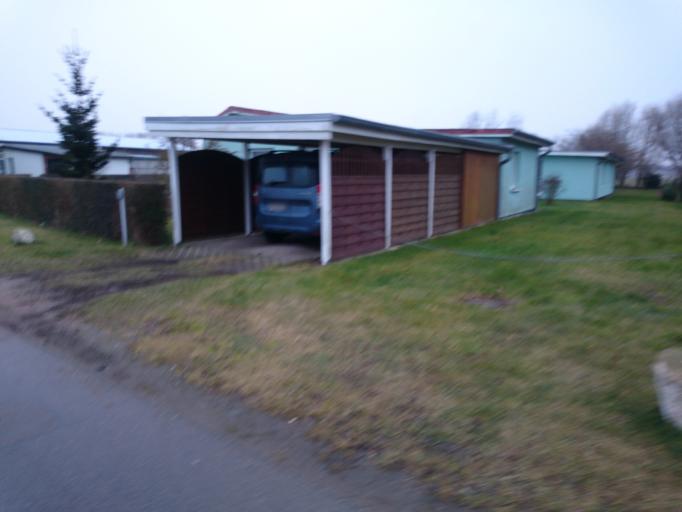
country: DE
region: Mecklenburg-Vorpommern
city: Elmenhorst
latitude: 54.1628
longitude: 11.9685
